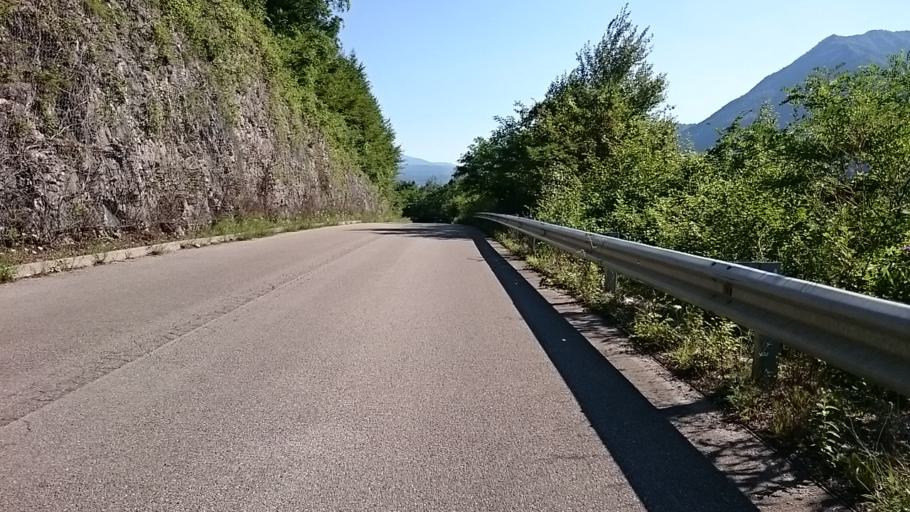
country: IT
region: Veneto
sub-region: Provincia di Belluno
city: Soverzene
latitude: 46.2286
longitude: 12.3019
